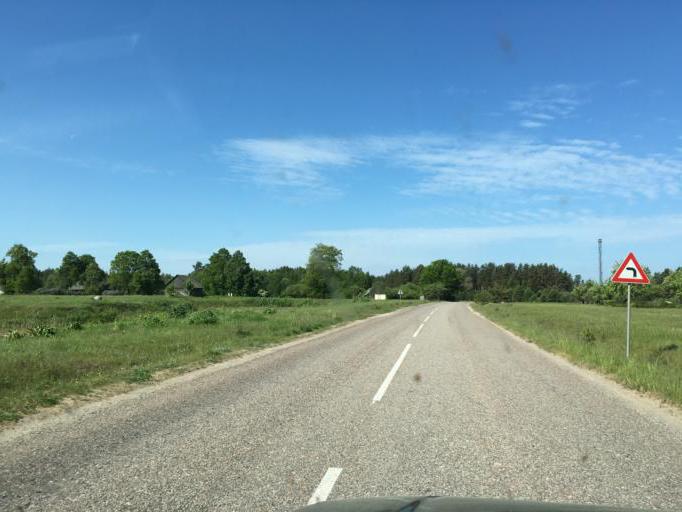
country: LV
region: Ventspils
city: Ventspils
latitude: 57.4822
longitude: 21.7656
